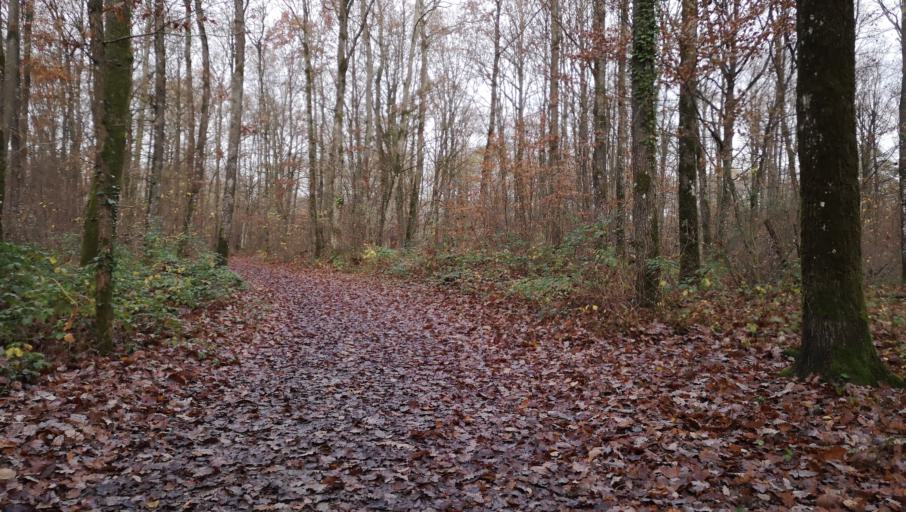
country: FR
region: Centre
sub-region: Departement du Loiret
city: Semoy
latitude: 47.9453
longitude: 1.9518
